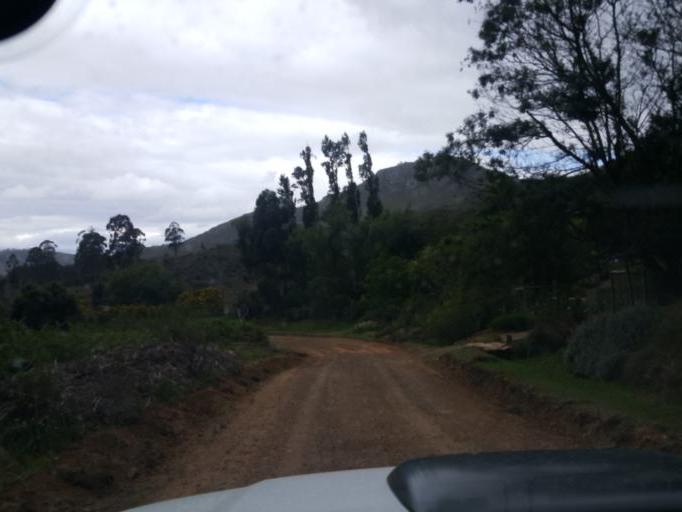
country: ZA
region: Western Cape
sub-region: Eden District Municipality
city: George
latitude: -33.8790
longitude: 22.4394
